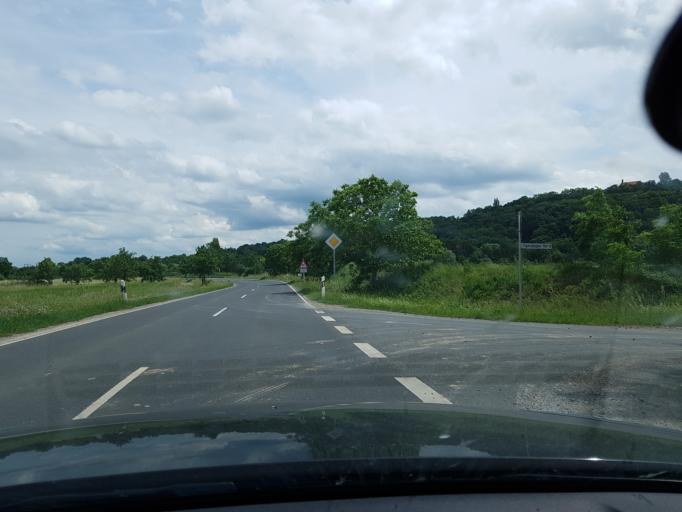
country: DE
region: Bavaria
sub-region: Regierungsbezirk Unterfranken
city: Nordheim
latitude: 49.8737
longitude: 10.1795
